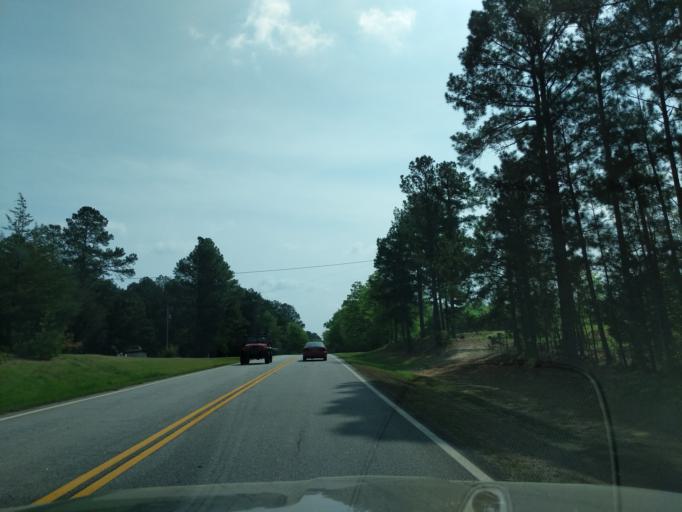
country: US
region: Georgia
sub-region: Lincoln County
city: Lincolnton
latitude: 33.8057
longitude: -82.4049
